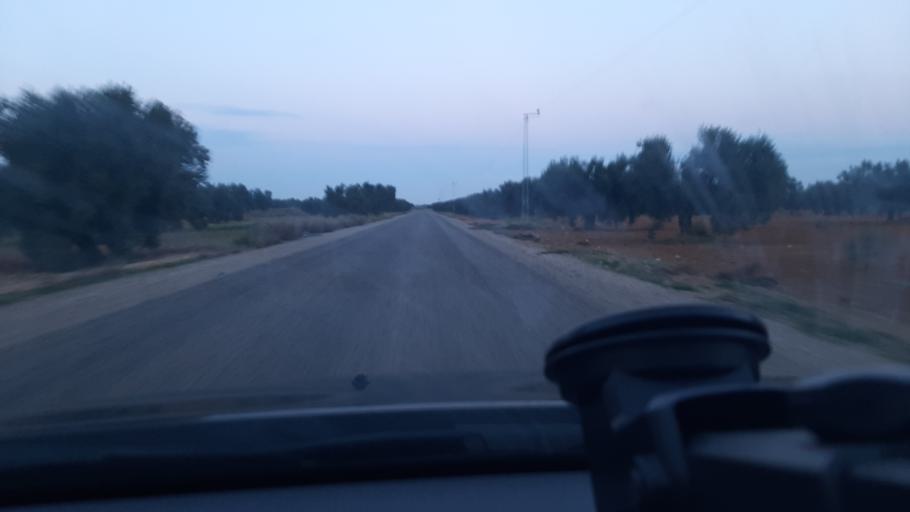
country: TN
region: Al Mahdiyah
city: Shurban
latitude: 35.0256
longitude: 10.4740
